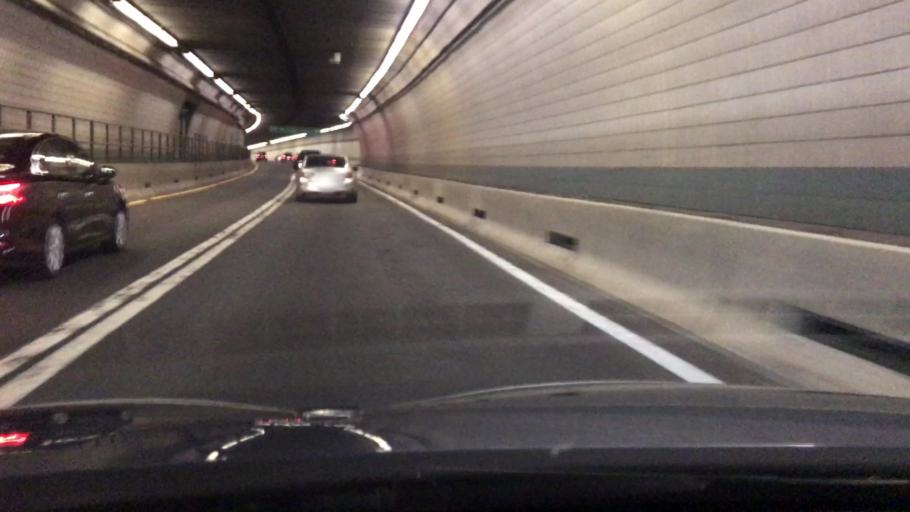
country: US
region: Massachusetts
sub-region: Suffolk County
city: South Boston
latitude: 42.3479
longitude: -71.0285
